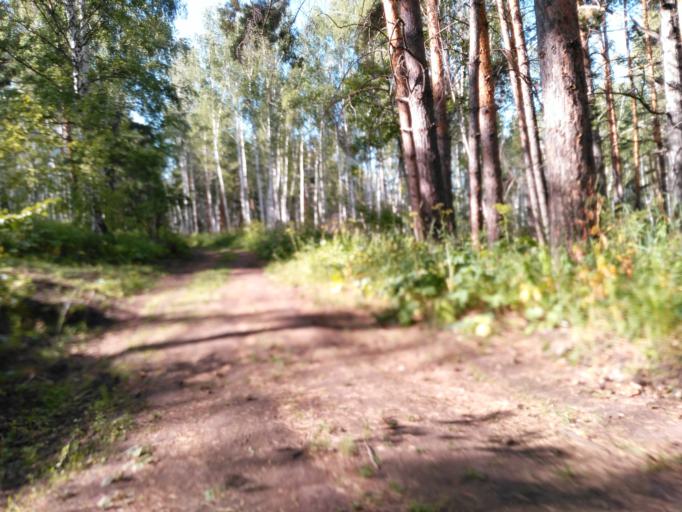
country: RU
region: Bashkortostan
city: Uchaly
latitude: 54.3300
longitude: 59.3584
